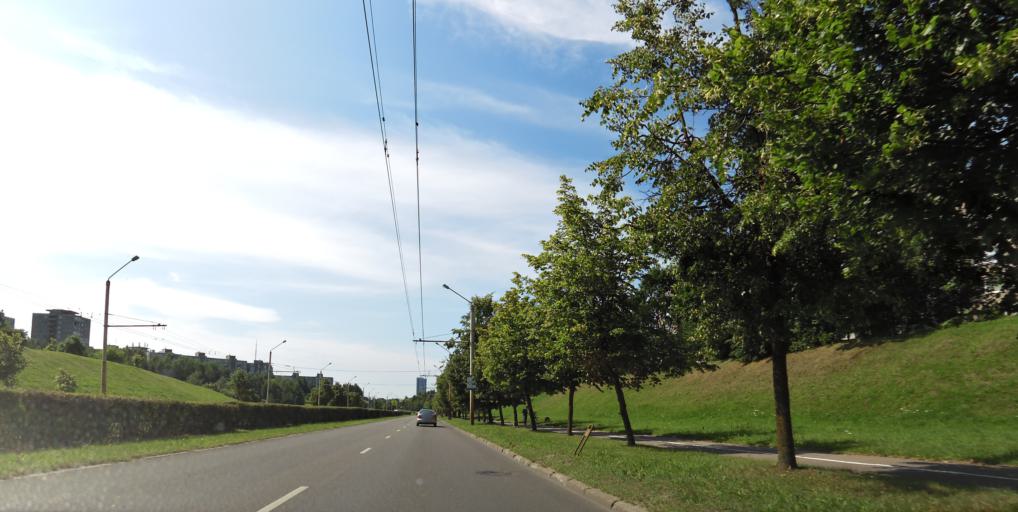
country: LT
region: Vilnius County
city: Justiniskes
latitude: 54.7137
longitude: 25.2189
